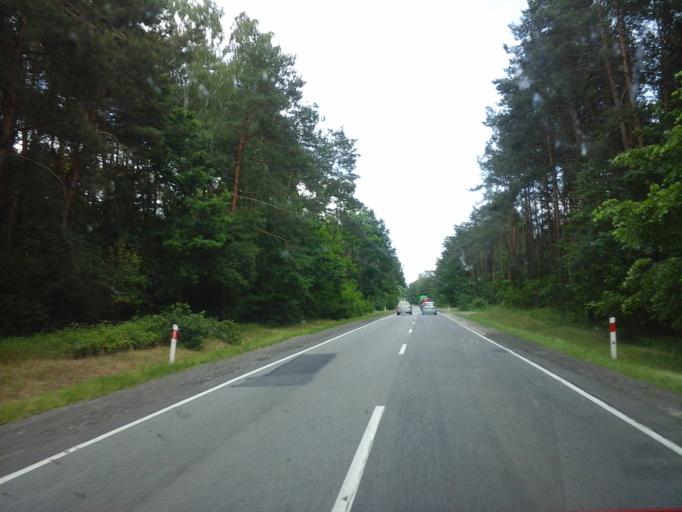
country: PL
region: Lodz Voivodeship
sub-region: Powiat opoczynski
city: Paradyz
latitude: 51.3106
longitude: 20.0891
